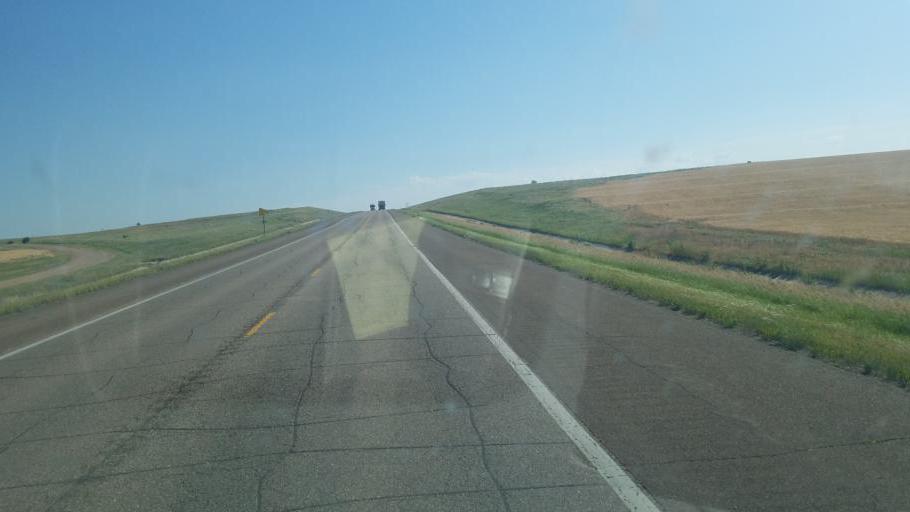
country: US
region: Kansas
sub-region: Barton County
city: Great Bend
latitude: 38.3824
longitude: -98.6829
